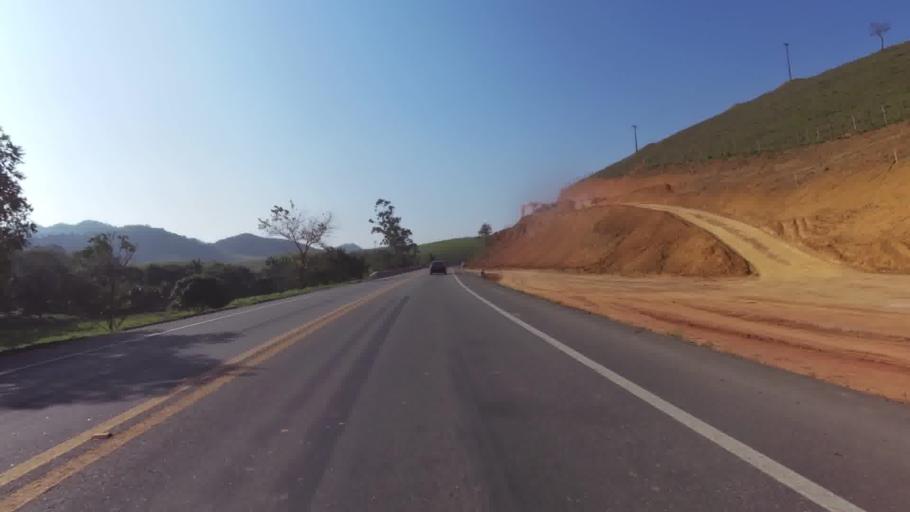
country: BR
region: Espirito Santo
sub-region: Iconha
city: Iconha
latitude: -20.7387
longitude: -40.7606
